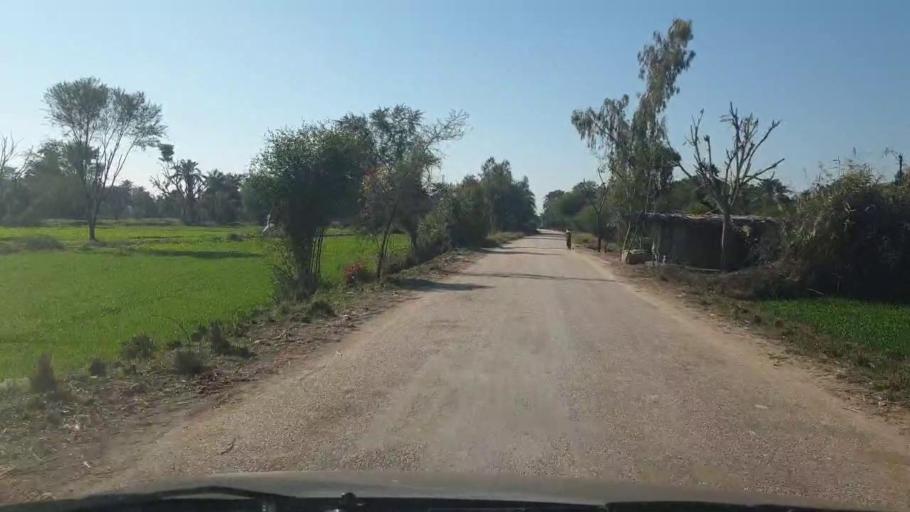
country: PK
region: Sindh
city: Bozdar
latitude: 27.1504
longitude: 68.6524
